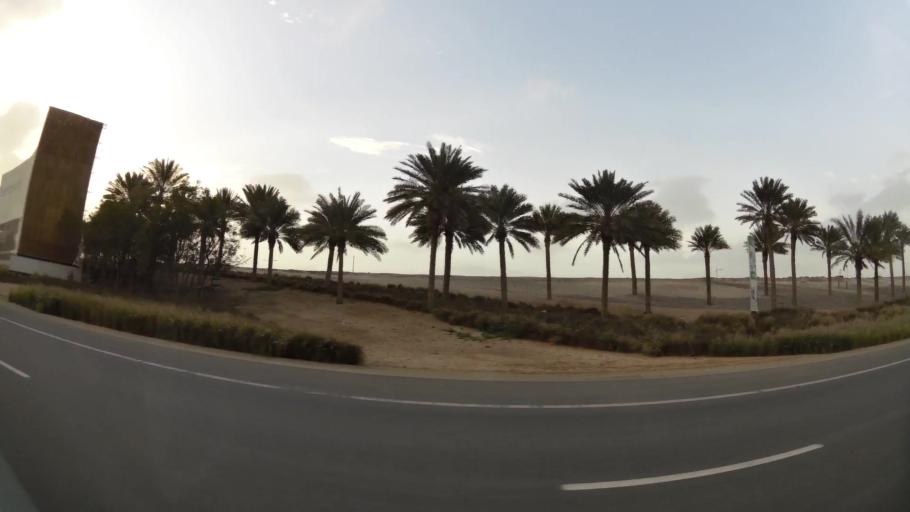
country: AE
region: Abu Dhabi
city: Abu Dhabi
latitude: 24.5290
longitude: 54.4116
